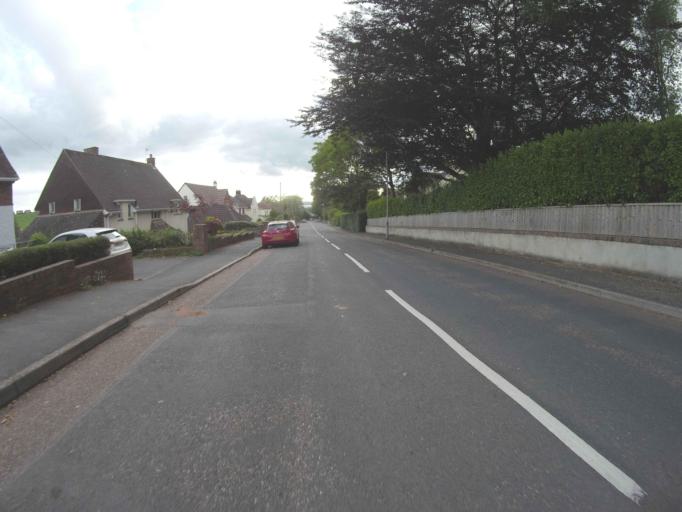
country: GB
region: England
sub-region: Devon
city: Exmouth
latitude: 50.6180
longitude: -3.3909
